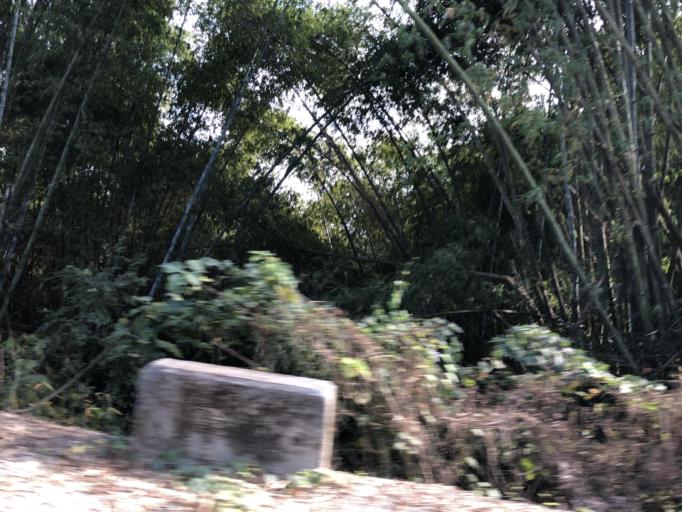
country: TW
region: Taiwan
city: Yujing
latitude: 23.0319
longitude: 120.3937
